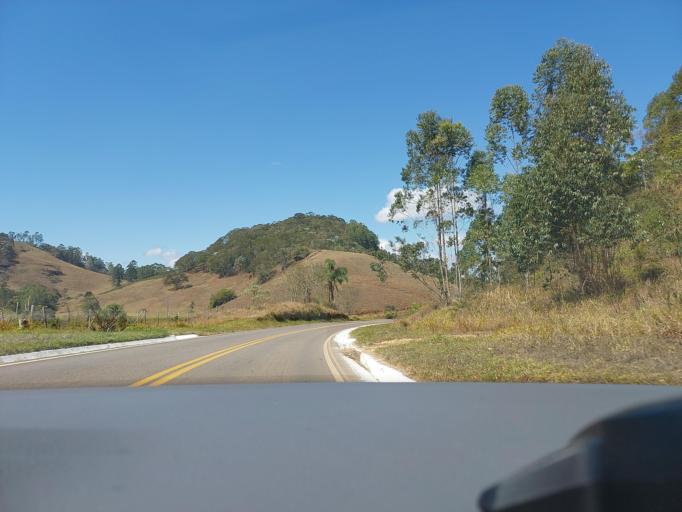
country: BR
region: Minas Gerais
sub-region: Mirai
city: Mirai
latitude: -21.0148
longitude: -42.5428
